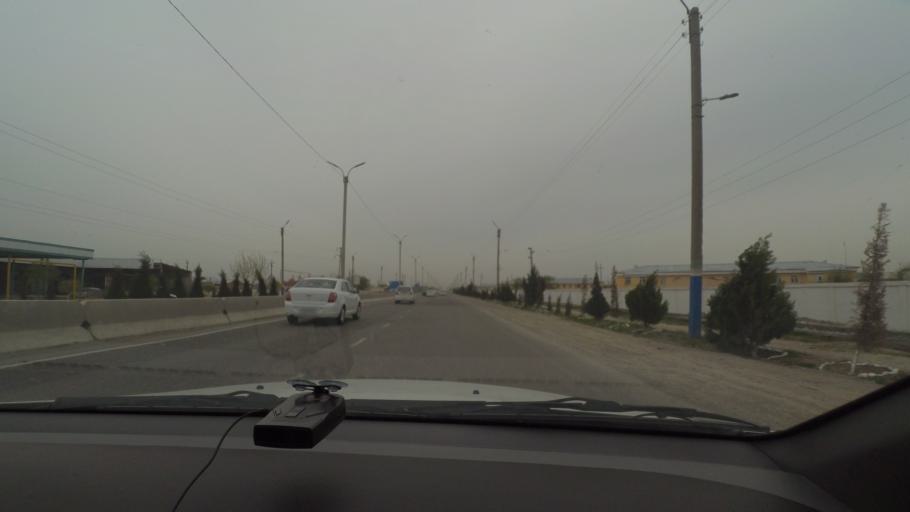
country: KZ
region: Ongtustik Qazaqstan
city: Myrzakent
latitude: 40.5467
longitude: 68.4089
